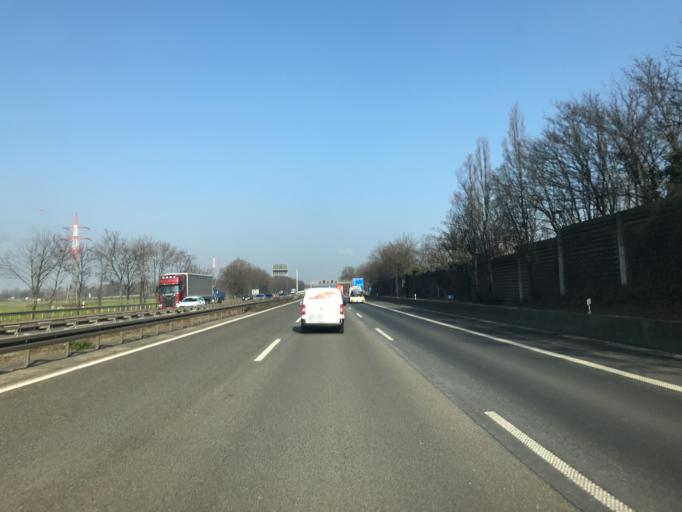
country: DE
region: North Rhine-Westphalia
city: Wesseling
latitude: 50.8561
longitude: 6.9688
